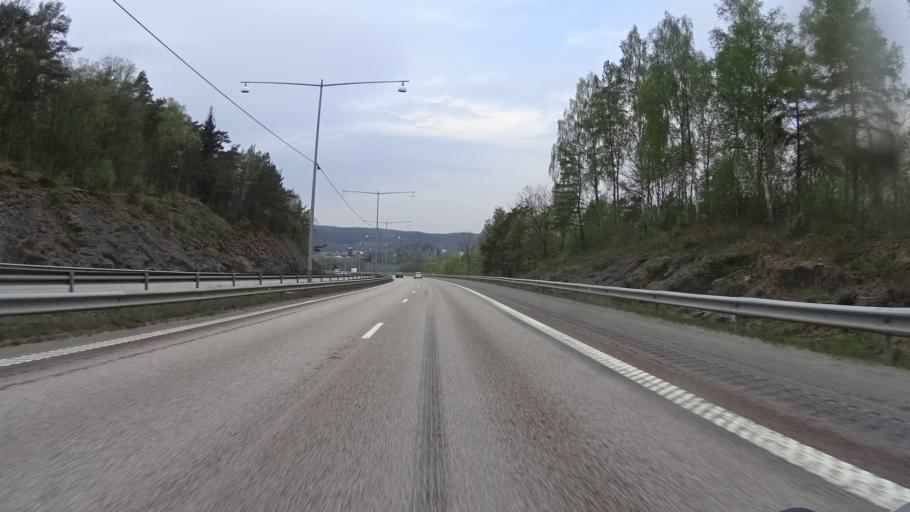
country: SE
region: Vaestra Goetaland
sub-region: Partille Kommun
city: Furulund
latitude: 57.7422
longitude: 12.1669
